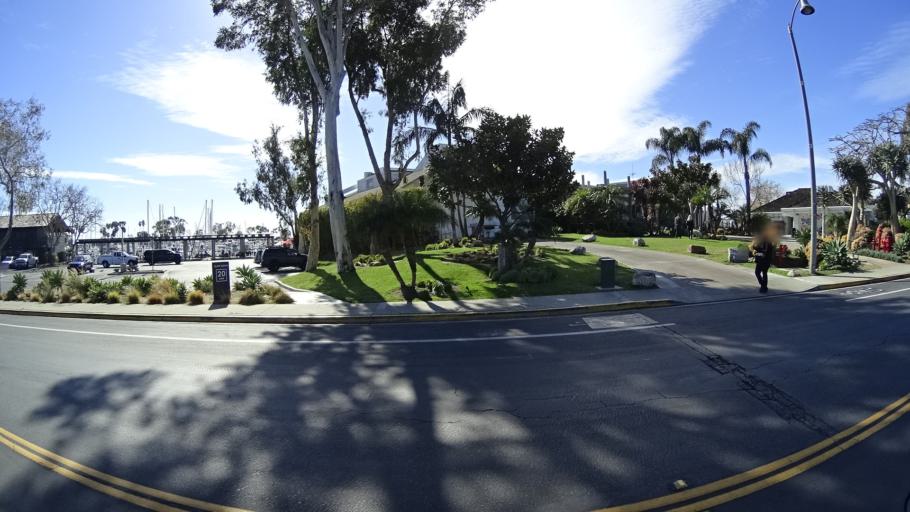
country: US
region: California
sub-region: Orange County
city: Dana Point
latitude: 33.4611
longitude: -117.6940
